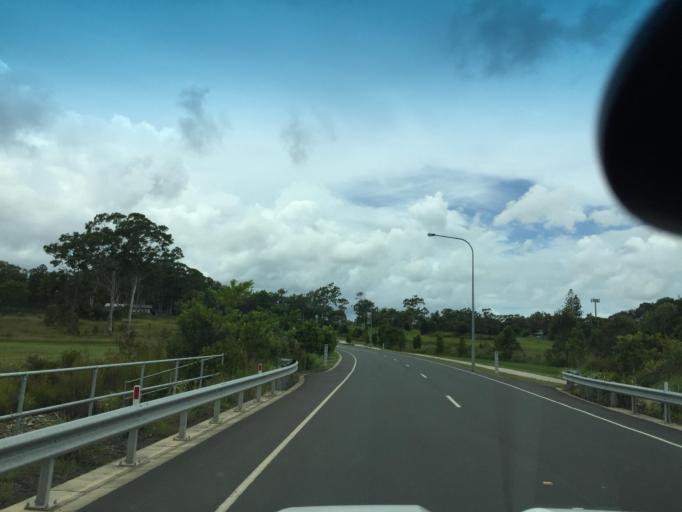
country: AU
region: Queensland
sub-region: Moreton Bay
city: Caboolture
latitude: -27.0591
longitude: 152.9381
